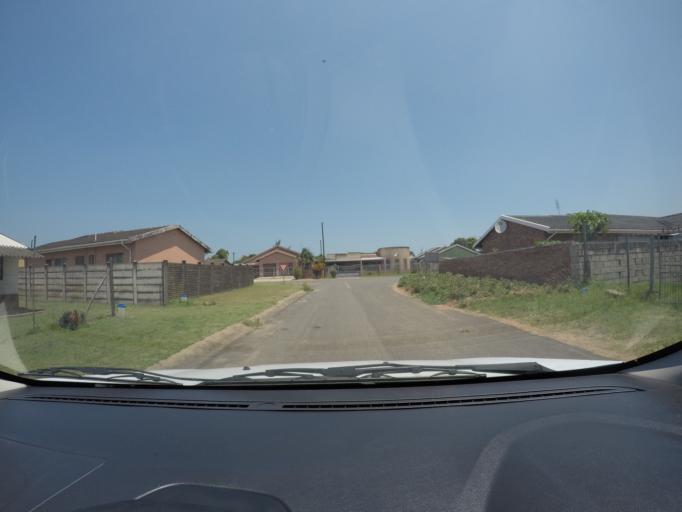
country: ZA
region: KwaZulu-Natal
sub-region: uThungulu District Municipality
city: eSikhawini
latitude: -28.8919
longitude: 31.8866
